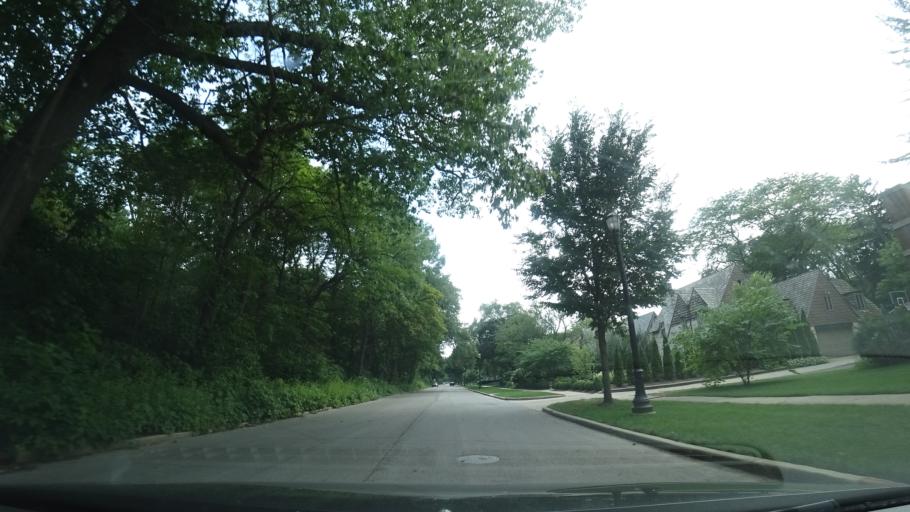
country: US
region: Illinois
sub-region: Cook County
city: Wilmette
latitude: 42.0605
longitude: -87.7130
